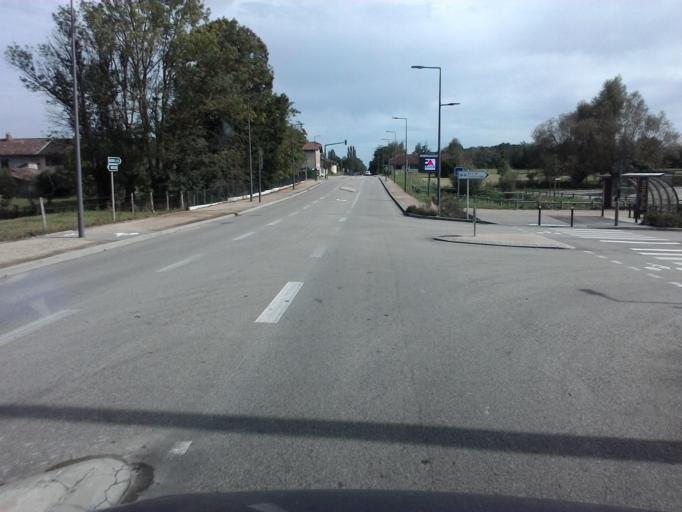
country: FR
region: Rhone-Alpes
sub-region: Departement de l'Ain
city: Mezeriat
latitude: 46.2558
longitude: 5.0599
